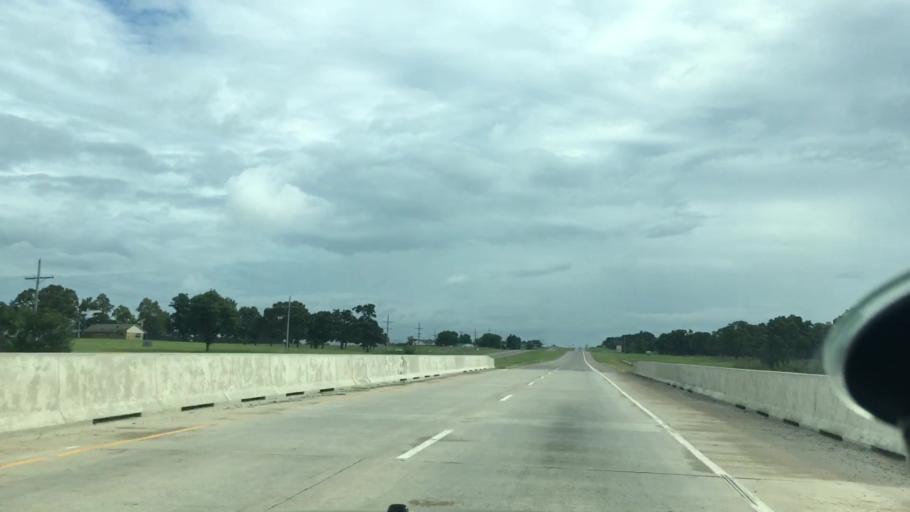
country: US
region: Oklahoma
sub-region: Lincoln County
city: Prague
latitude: 35.3607
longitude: -96.6718
